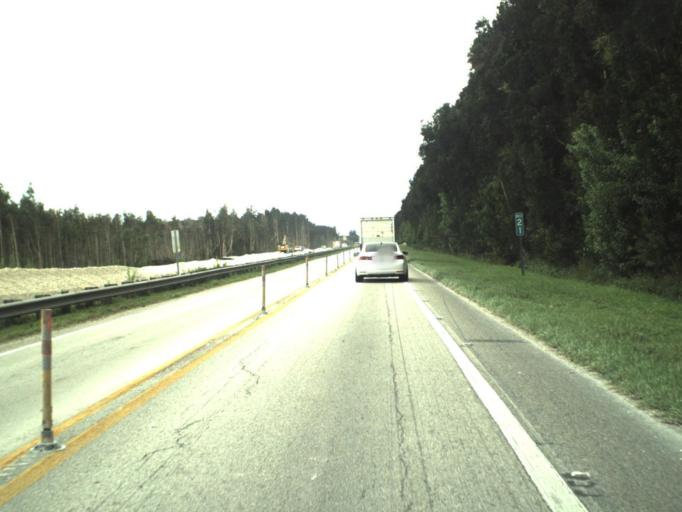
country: US
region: Florida
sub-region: Miami-Dade County
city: Kendall West
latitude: 25.7408
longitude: -80.4806
